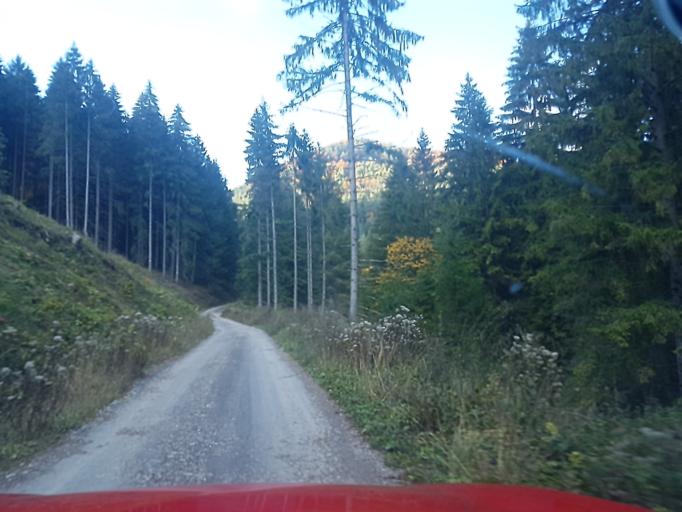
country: SK
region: Zilinsky
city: Ruzomberok
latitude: 49.1133
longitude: 19.3738
